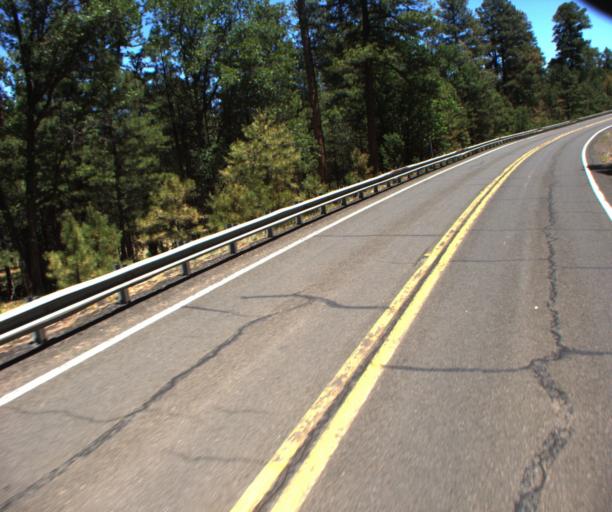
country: US
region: Arizona
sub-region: Gila County
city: Pine
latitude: 34.6067
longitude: -111.2300
